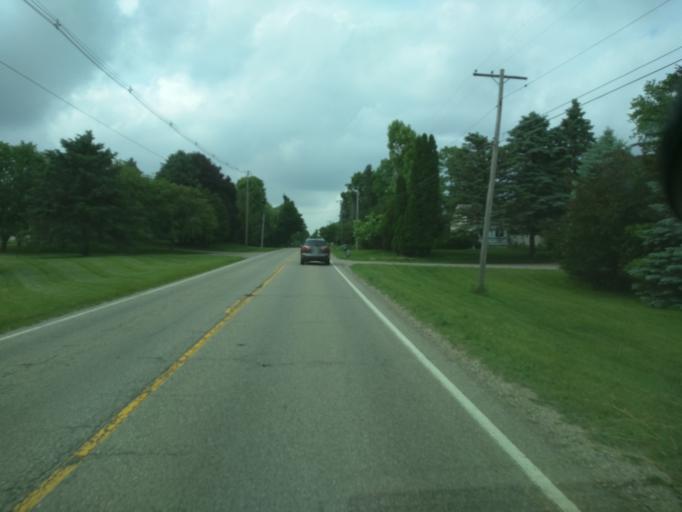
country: US
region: Michigan
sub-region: Ingham County
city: Edgemont Park
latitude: 42.7902
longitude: -84.6028
